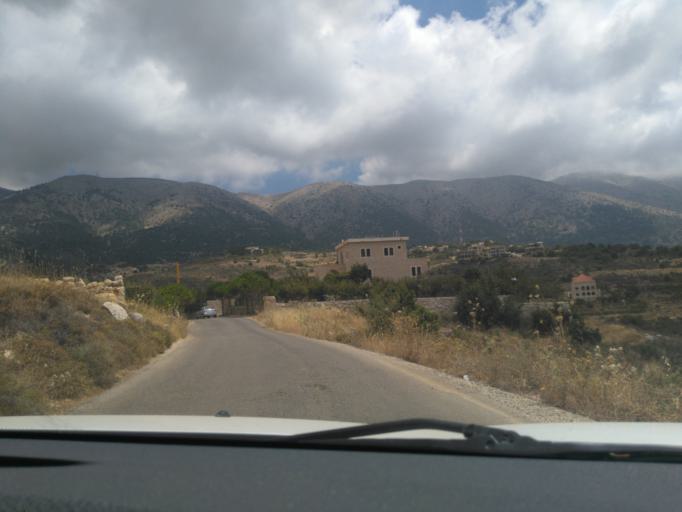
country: LB
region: Mont-Liban
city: Beit ed Dine
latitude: 33.6758
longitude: 35.6635
